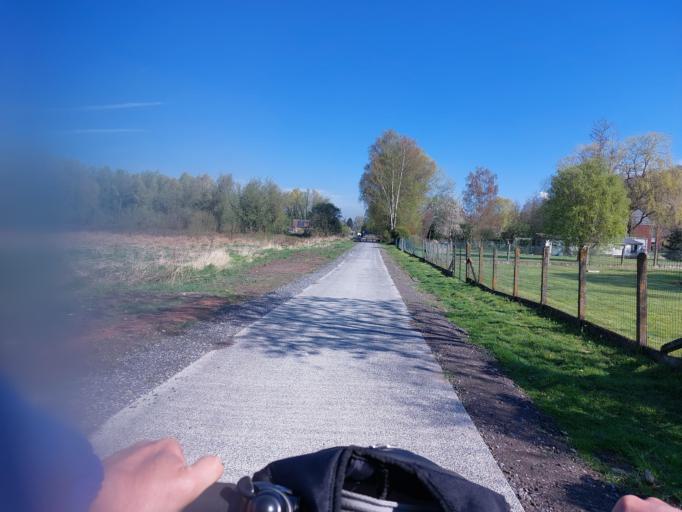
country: BE
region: Wallonia
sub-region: Province du Hainaut
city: Mons
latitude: 50.4453
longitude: 3.9693
